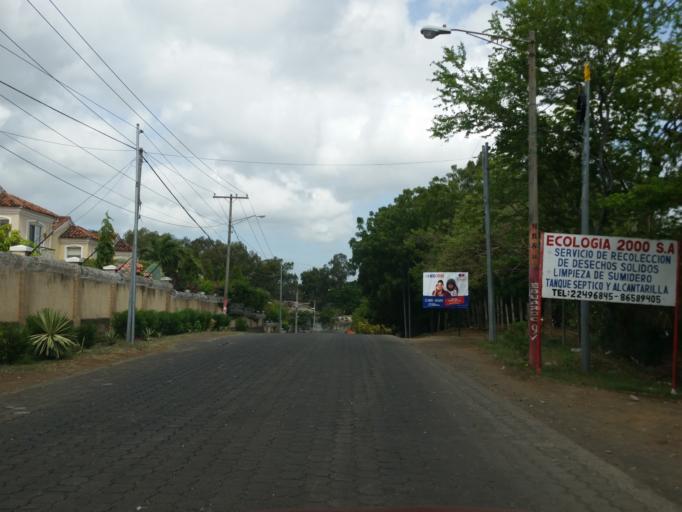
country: NI
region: Managua
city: Managua
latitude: 12.1149
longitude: -86.2750
